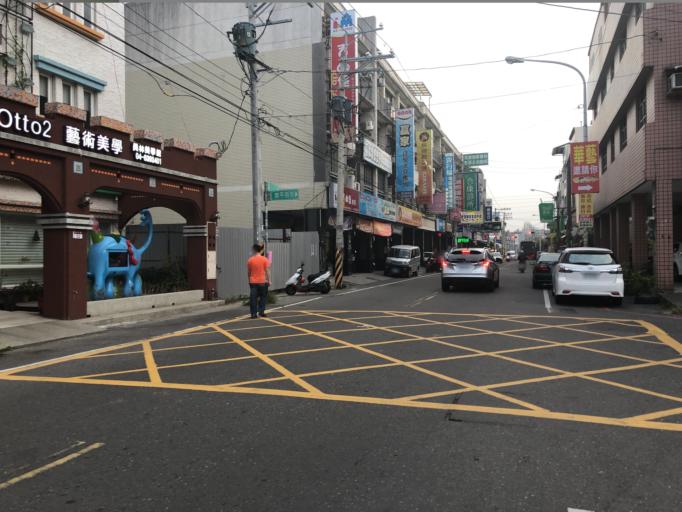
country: TW
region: Taiwan
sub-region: Changhua
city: Chang-hua
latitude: 23.9636
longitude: 120.5646
